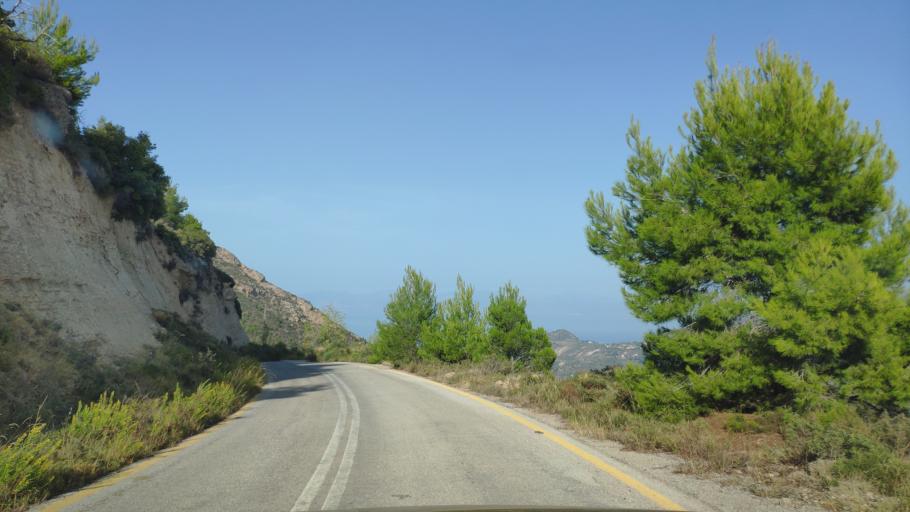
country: GR
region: West Greece
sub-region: Nomos Achaias
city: Aiyira
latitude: 38.0694
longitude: 22.3860
